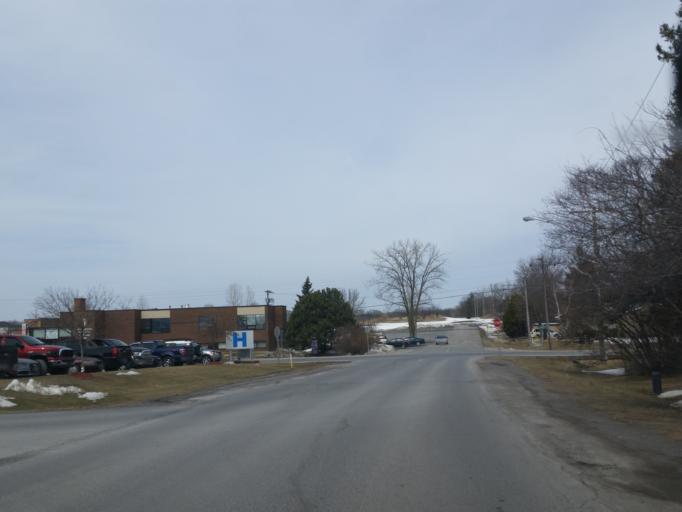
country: CA
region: Ontario
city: Napanee Downtown
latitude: 44.2404
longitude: -76.9659
